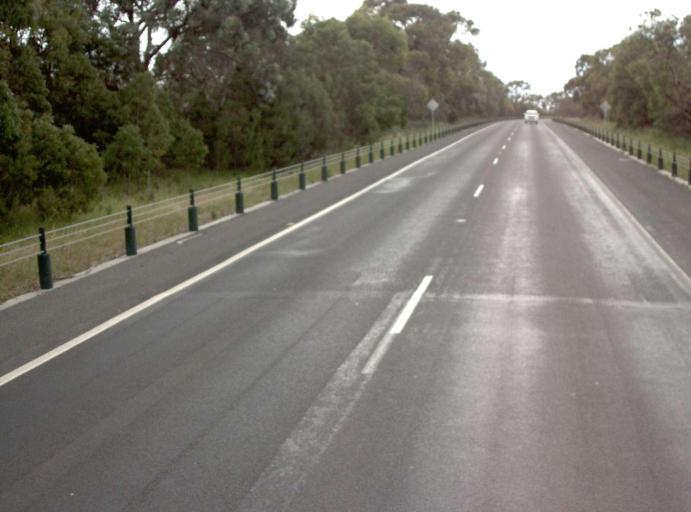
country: AU
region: Victoria
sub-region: Casey
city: Tooradin
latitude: -38.2166
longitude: 145.4023
